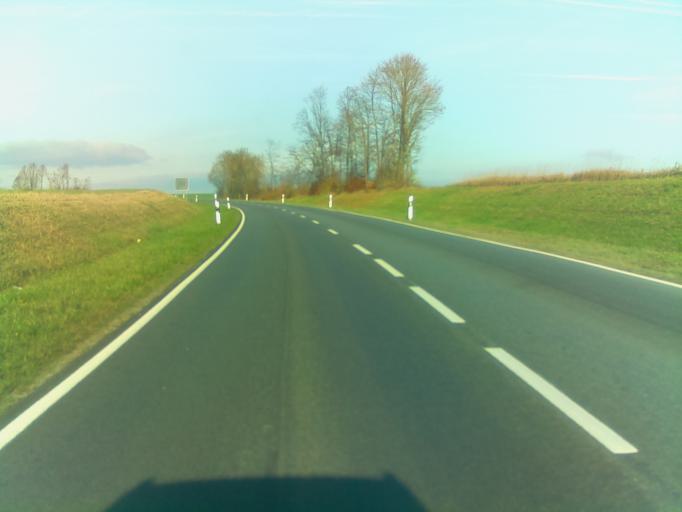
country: DE
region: Bavaria
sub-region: Regierungsbezirk Unterfranken
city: Kreuzwertheim
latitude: 49.8049
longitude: 9.5545
